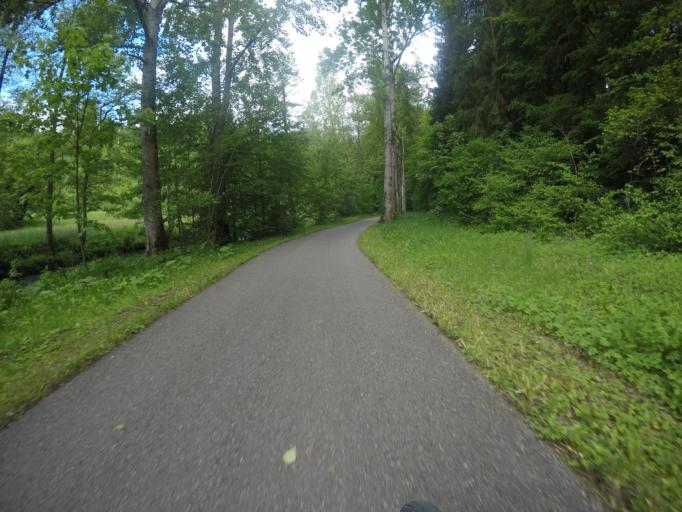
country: DE
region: Baden-Wuerttemberg
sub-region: Karlsruhe Region
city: Wildberg
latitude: 48.6040
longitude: 8.7373
